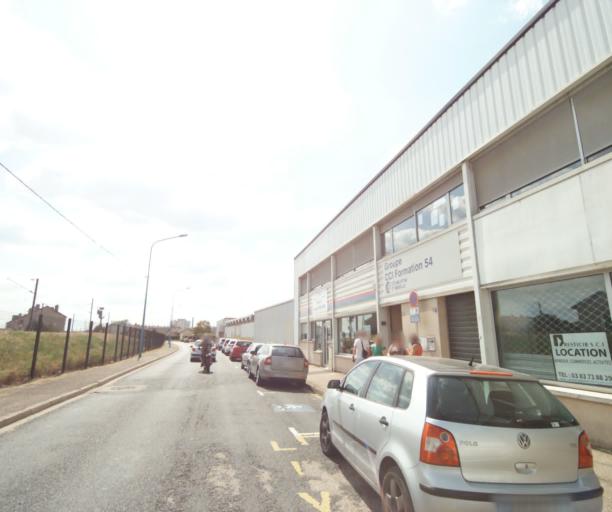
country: FR
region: Lorraine
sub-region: Departement de Meurthe-et-Moselle
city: Luneville
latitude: 48.5867
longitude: 6.4910
